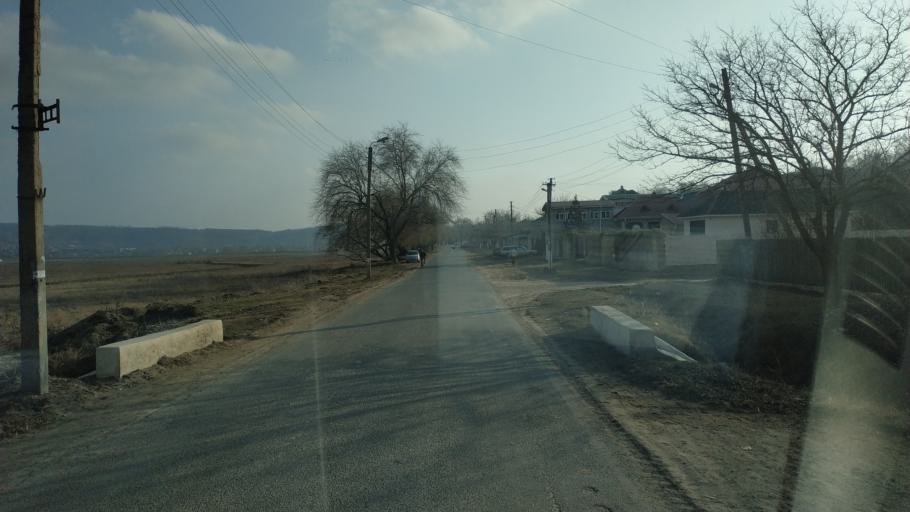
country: MD
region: Hincesti
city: Dancu
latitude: 46.7740
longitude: 28.3462
